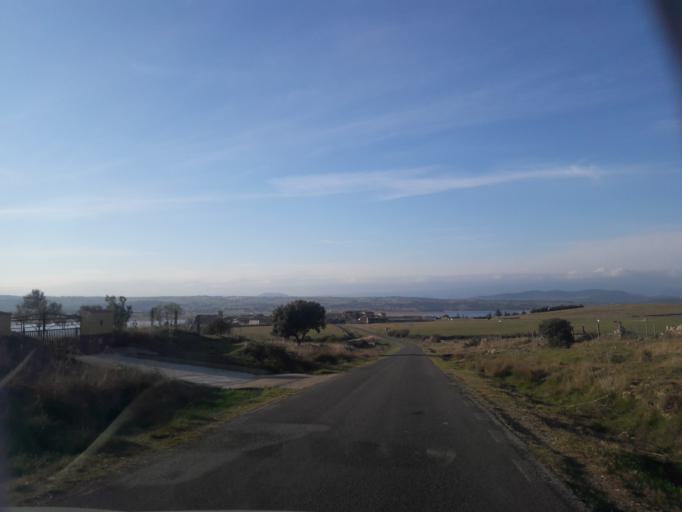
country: ES
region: Castille and Leon
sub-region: Provincia de Salamanca
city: Salvatierra de Tormes
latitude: 40.5959
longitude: -5.5993
